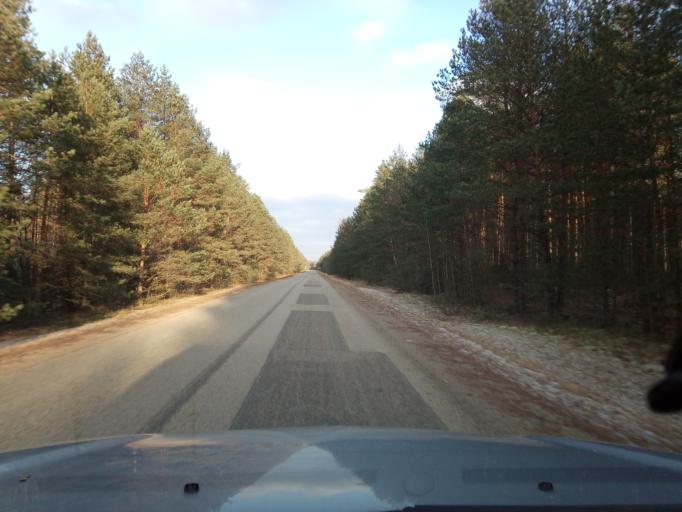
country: LT
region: Alytaus apskritis
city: Varena
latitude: 54.1561
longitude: 24.4901
